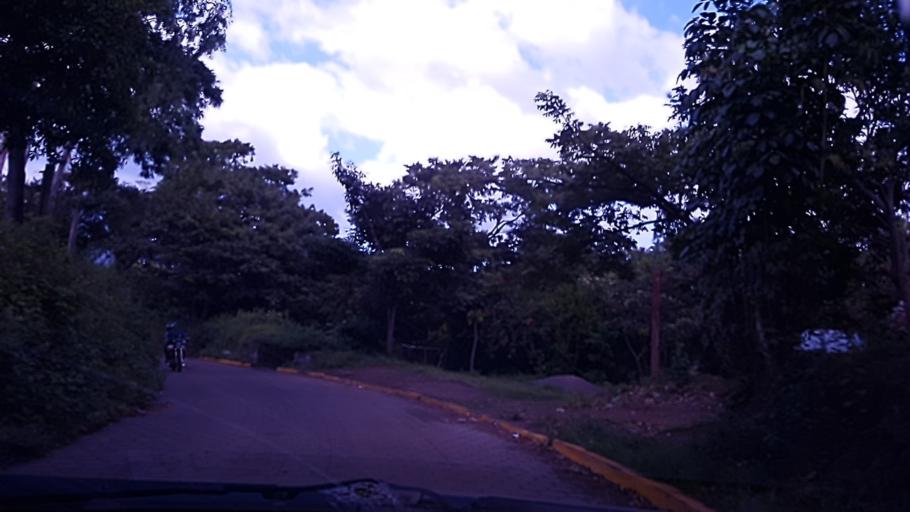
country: NI
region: Masaya
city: Ticuantepe
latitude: 11.9931
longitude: -86.2245
